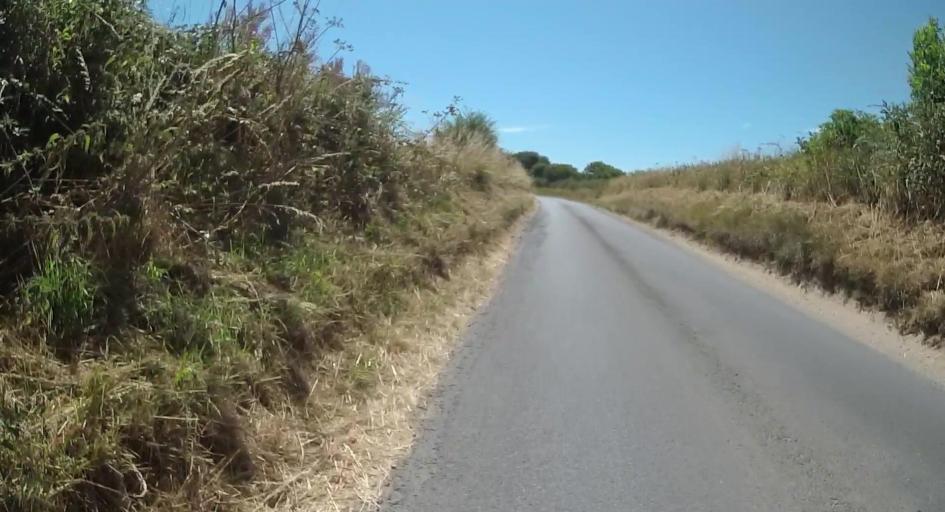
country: GB
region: England
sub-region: Dorset
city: Bovington Camp
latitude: 50.6530
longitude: -2.2855
